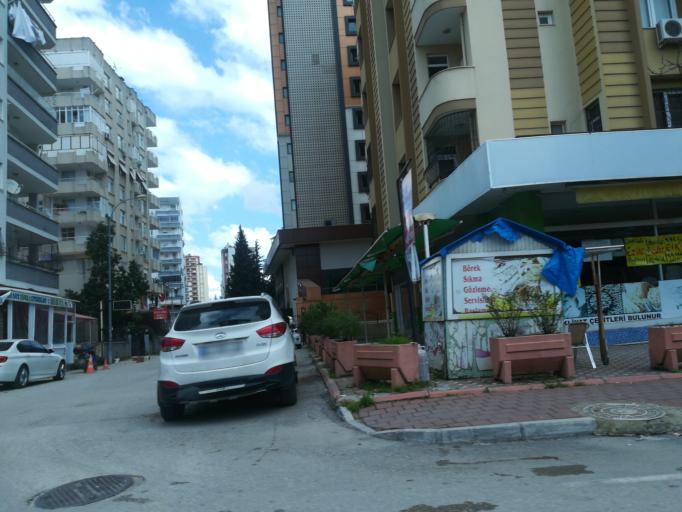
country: TR
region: Adana
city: Adana
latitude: 37.0337
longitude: 35.3127
